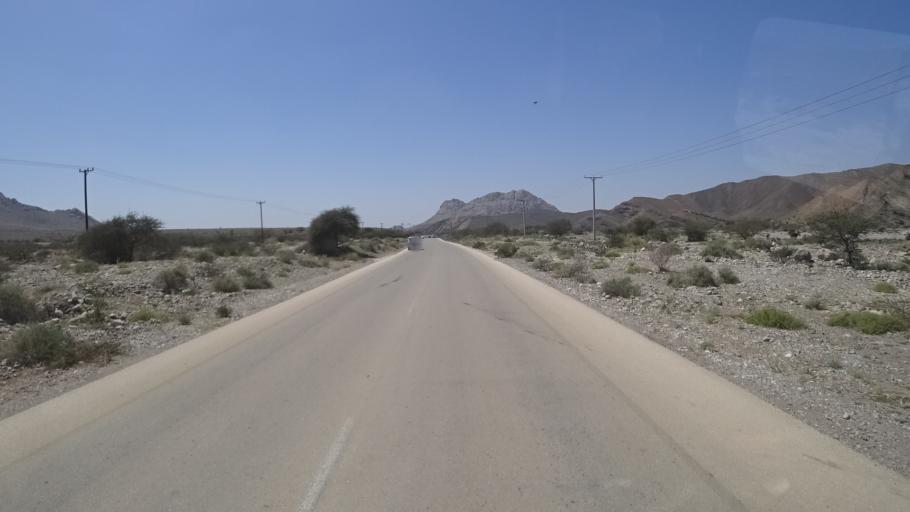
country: OM
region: Az Zahirah
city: `Ibri
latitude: 23.1940
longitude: 56.9303
